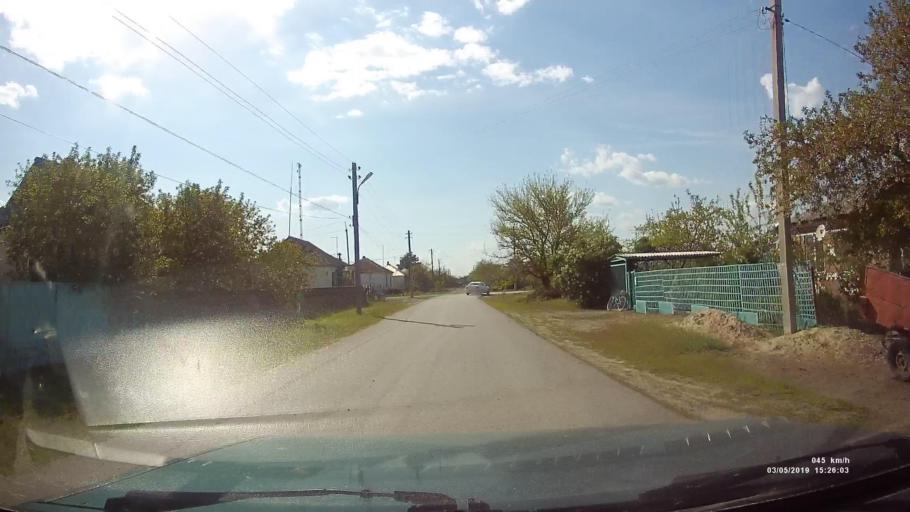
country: RU
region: Rostov
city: Ust'-Donetskiy
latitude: 47.5796
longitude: 40.8541
